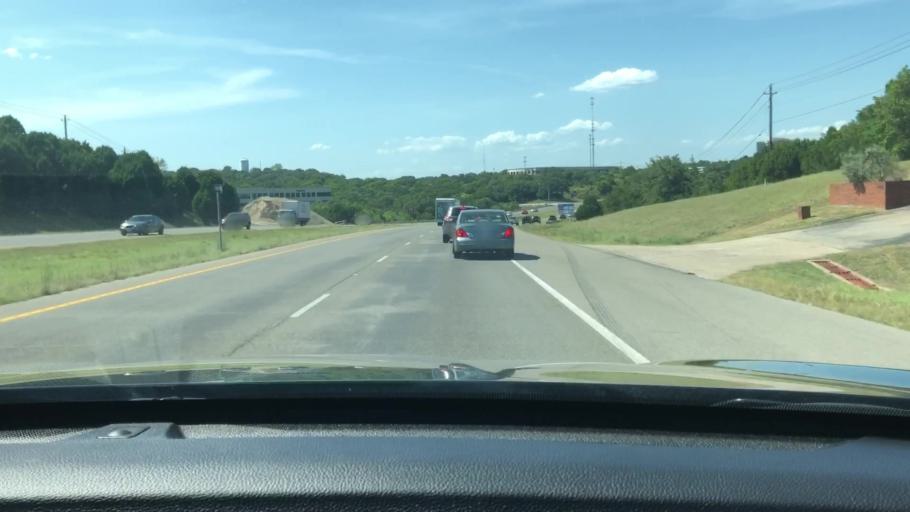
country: US
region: Texas
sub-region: Travis County
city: Lost Creek
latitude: 30.2873
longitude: -97.8267
